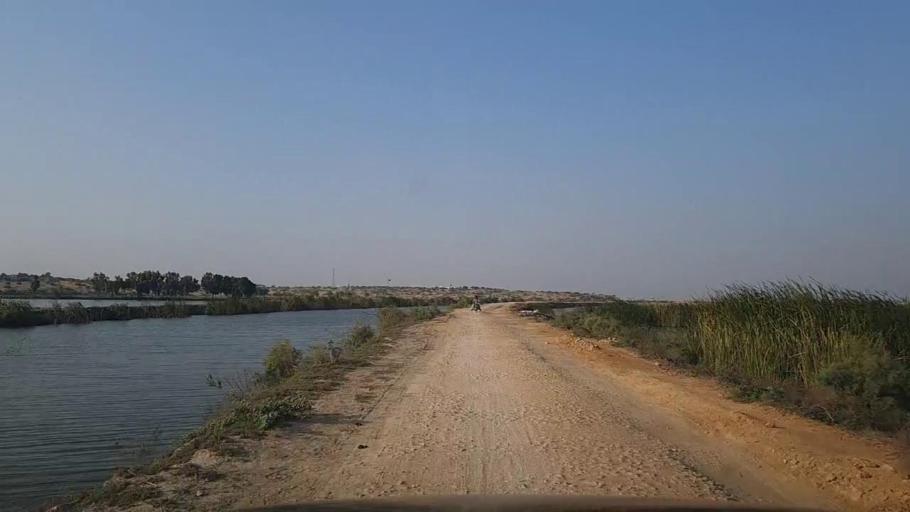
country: PK
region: Sindh
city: Thatta
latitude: 24.7346
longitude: 67.9066
